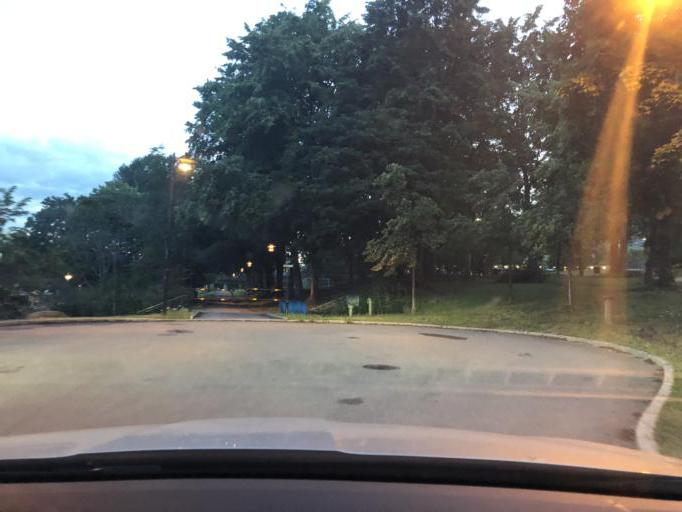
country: SE
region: Stockholm
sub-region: Botkyrka Kommun
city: Fittja
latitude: 59.2468
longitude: 17.8625
